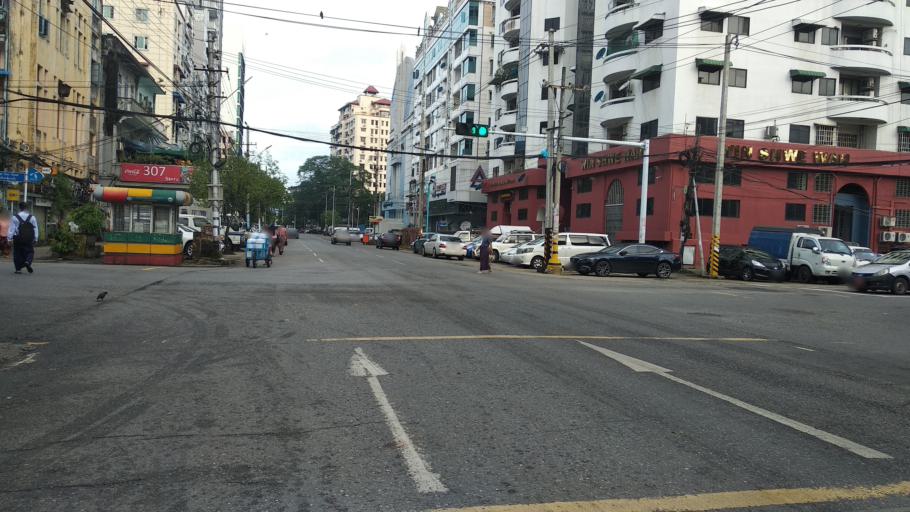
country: MM
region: Yangon
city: Yangon
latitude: 16.7776
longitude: 96.1397
